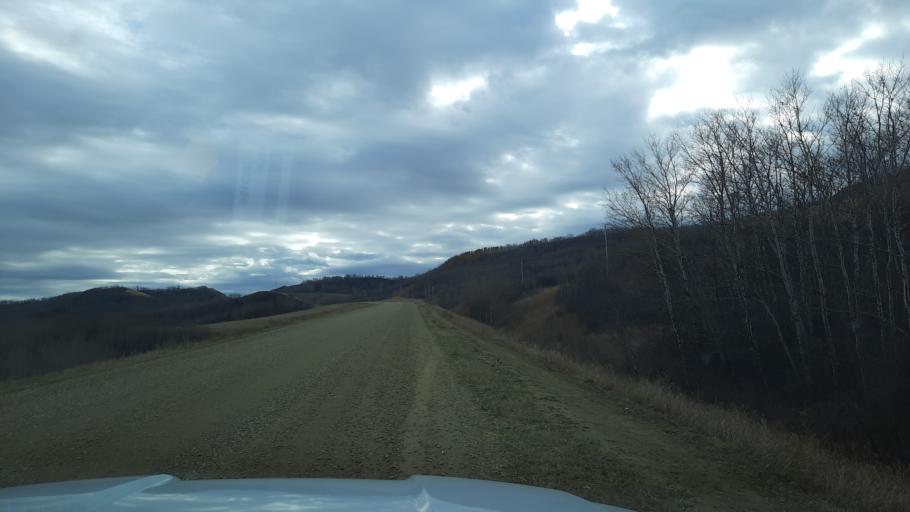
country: CA
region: Saskatchewan
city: Pilot Butte
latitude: 50.7736
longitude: -104.2820
